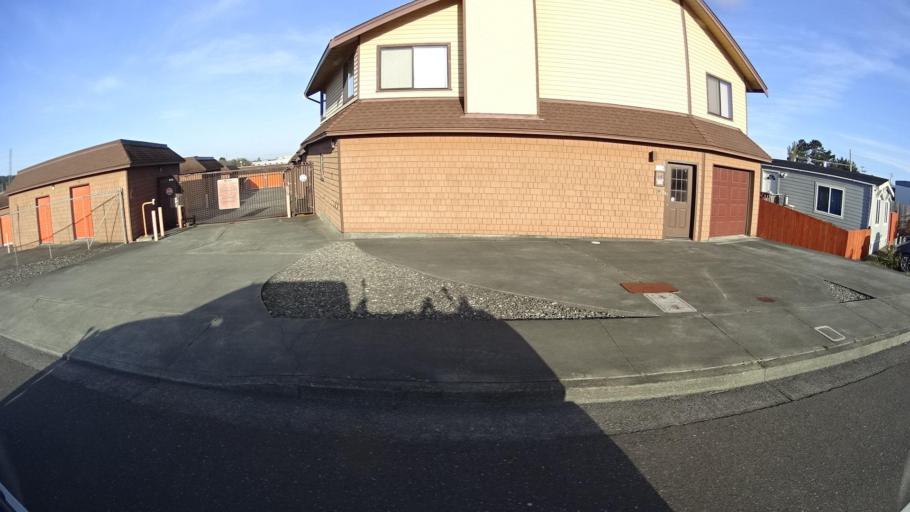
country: US
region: California
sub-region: Humboldt County
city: Humboldt Hill
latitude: 40.7404
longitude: -124.1994
